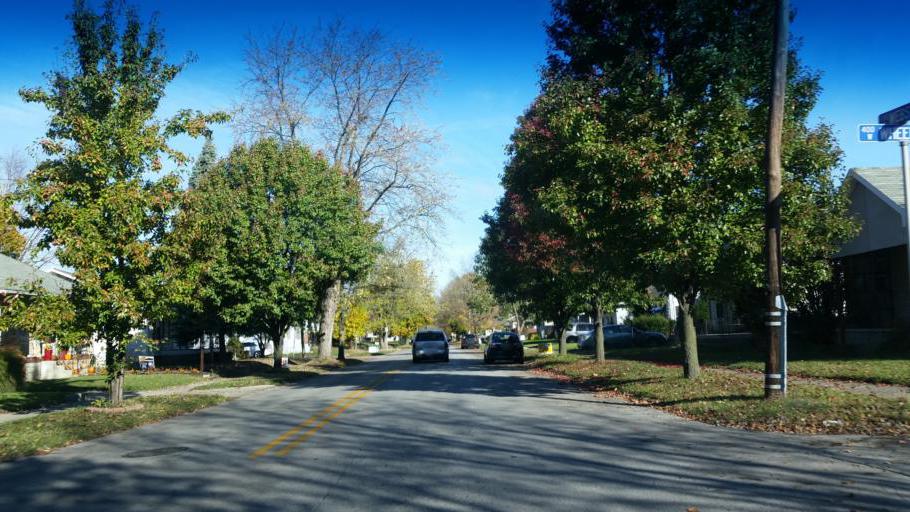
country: US
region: Indiana
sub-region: Howard County
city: Kokomo
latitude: 40.4669
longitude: -86.1364
